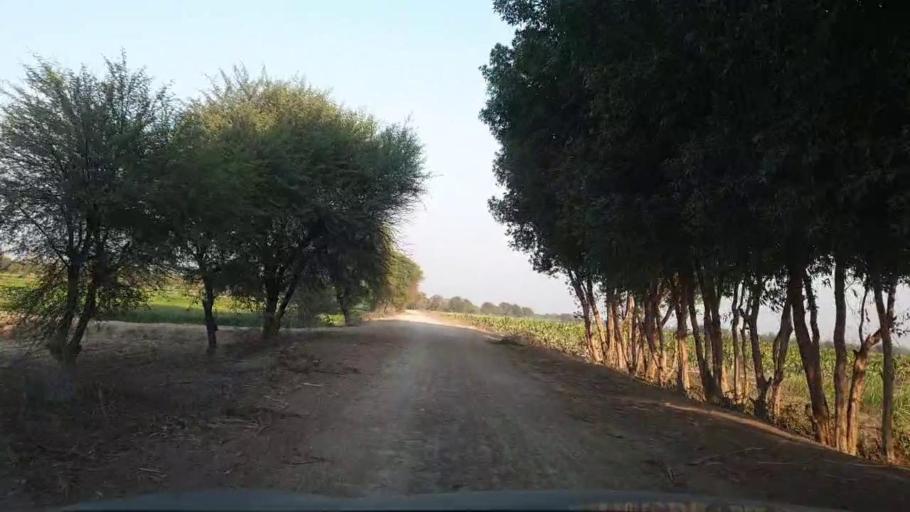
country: PK
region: Sindh
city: Mirpur Khas
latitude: 25.5543
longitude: 68.8577
